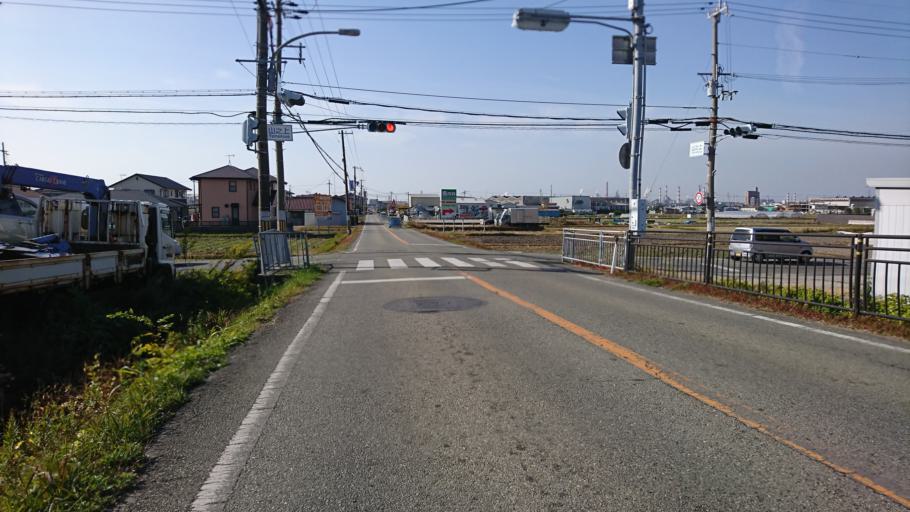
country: JP
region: Hyogo
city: Kakogawacho-honmachi
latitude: 34.7310
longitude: 134.8726
